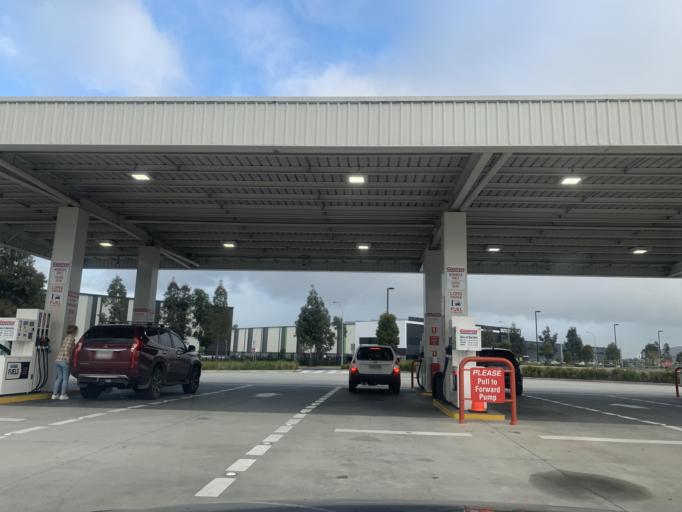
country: AU
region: Victoria
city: Heatherton
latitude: -37.9780
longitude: 145.1083
